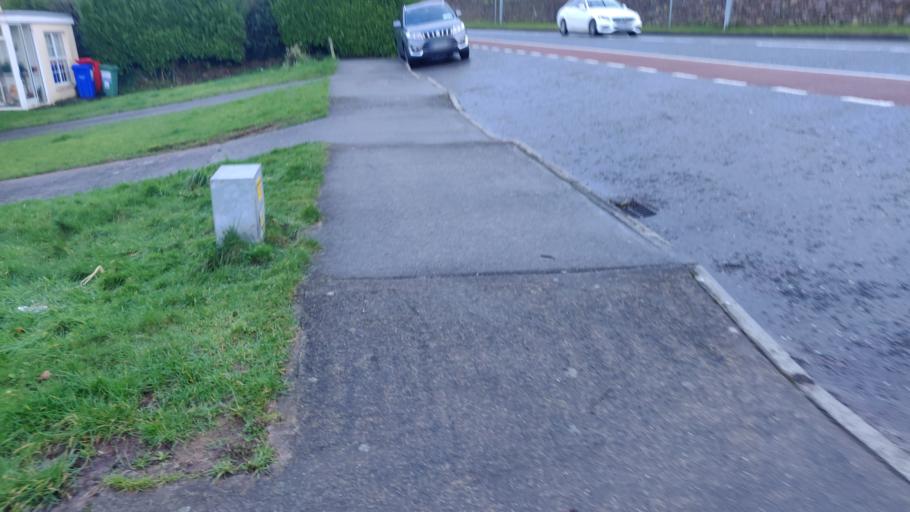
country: IE
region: Munster
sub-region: County Cork
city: Carrigaline
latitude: 51.8689
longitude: -8.4171
